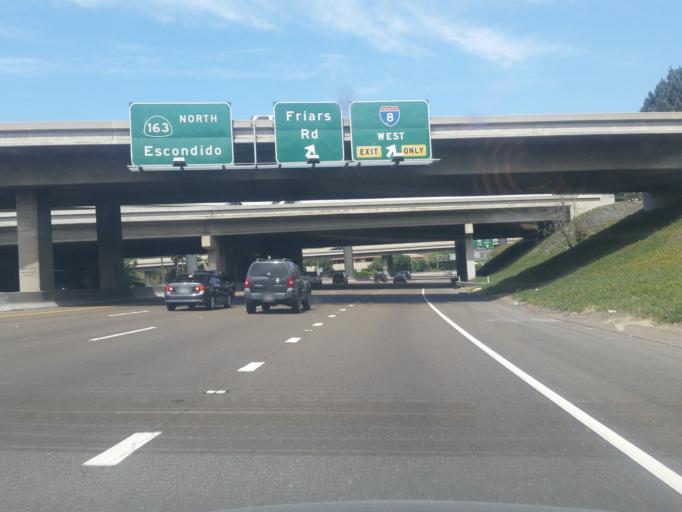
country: US
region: California
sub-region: San Diego County
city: San Diego
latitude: 32.7619
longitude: -117.1632
